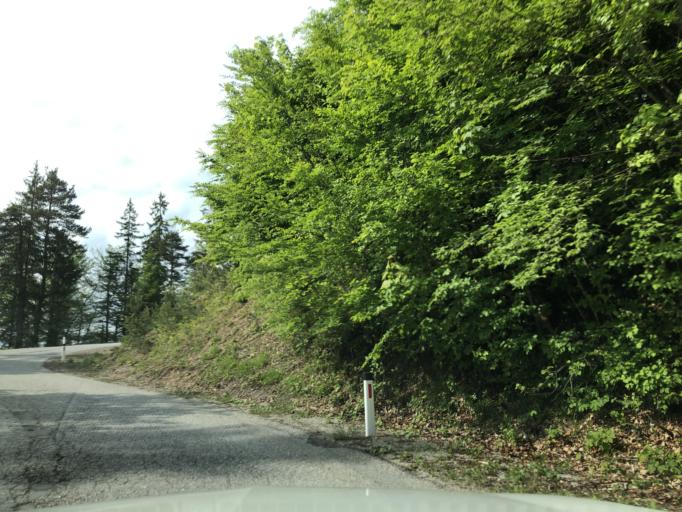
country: SI
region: Bloke
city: Nova Vas
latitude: 45.7991
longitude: 14.5552
